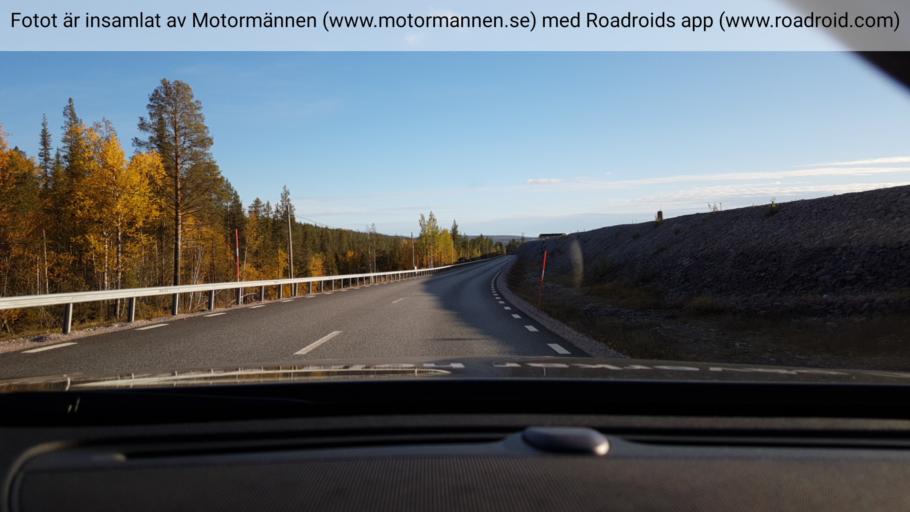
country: SE
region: Norrbotten
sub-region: Jokkmokks Kommun
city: Jokkmokk
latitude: 66.8905
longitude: 19.8284
